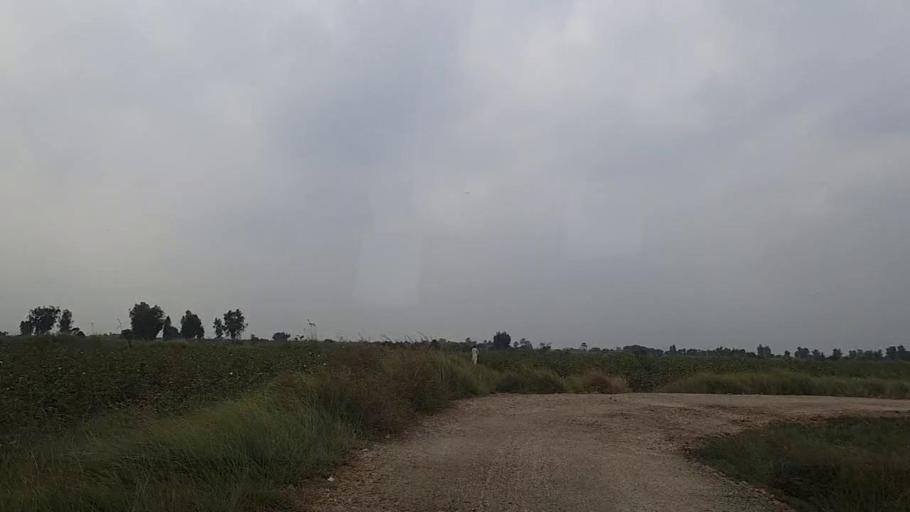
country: PK
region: Sindh
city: Mirpur Sakro
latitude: 24.6191
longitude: 67.7179
